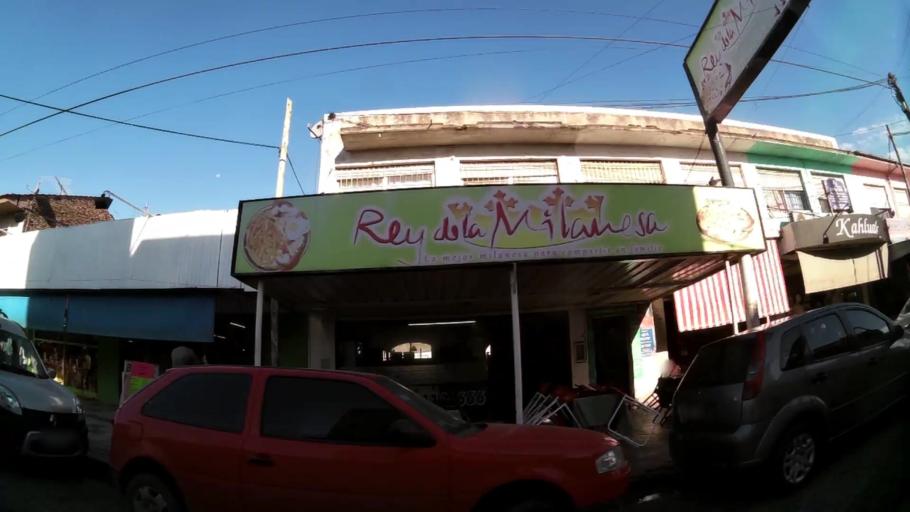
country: AR
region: Buenos Aires
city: Santa Catalina - Dique Lujan
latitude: -34.4883
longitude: -58.7263
